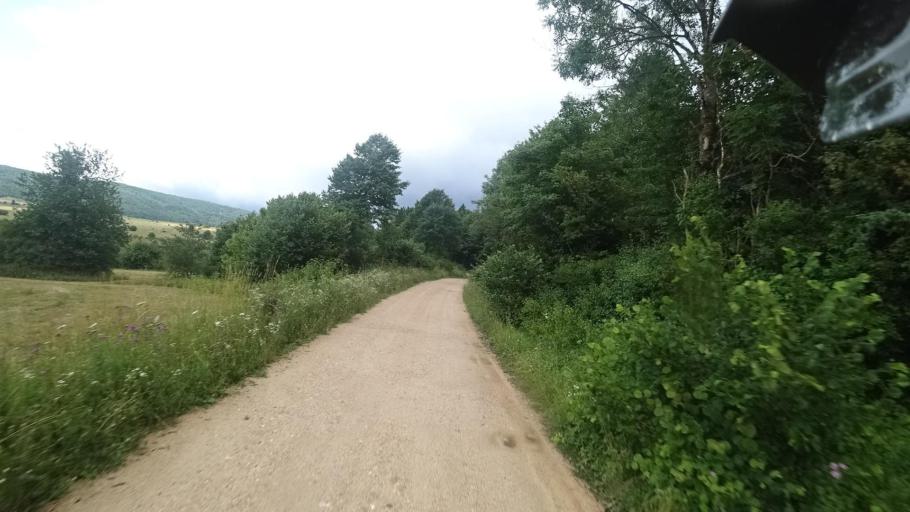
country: HR
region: Licko-Senjska
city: Jezerce
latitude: 44.7581
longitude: 15.6310
